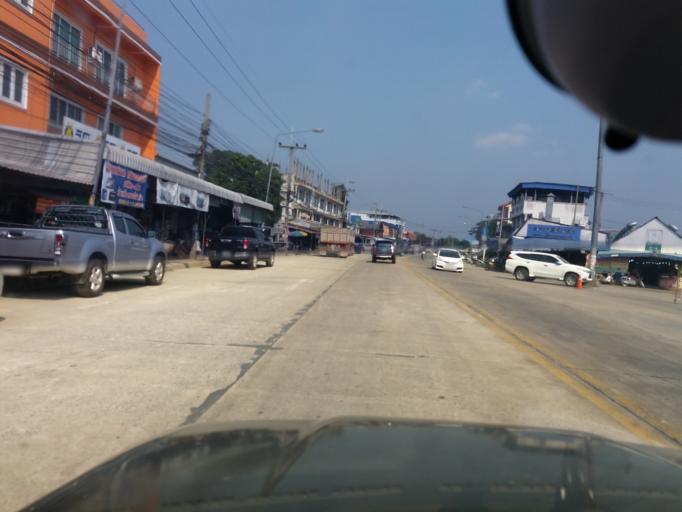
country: TH
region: Sing Buri
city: Bang Racham
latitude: 14.8871
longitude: 100.3147
